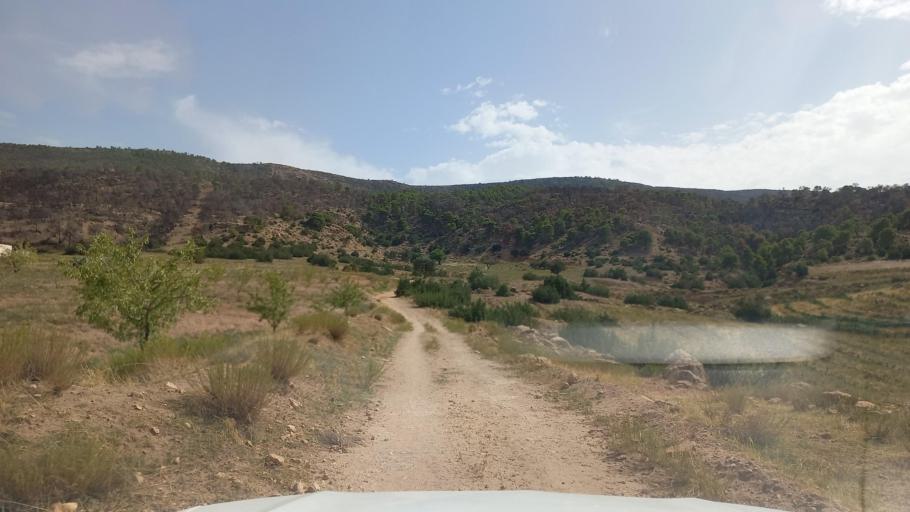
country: TN
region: Al Qasrayn
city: Kasserine
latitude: 35.3550
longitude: 8.8897
